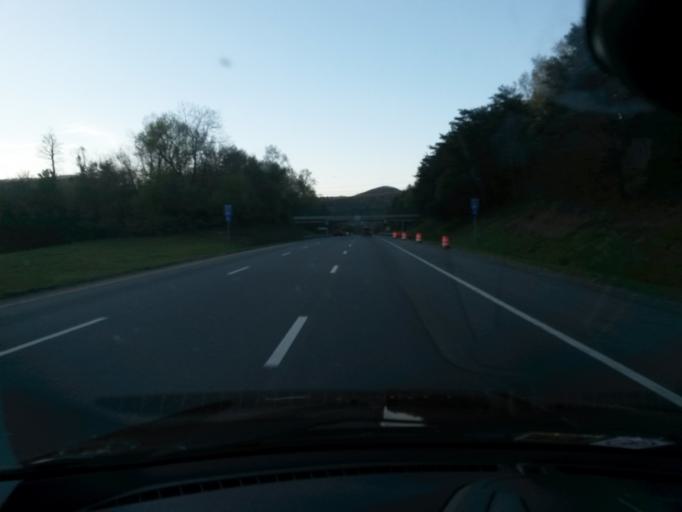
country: US
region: Virginia
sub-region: Roanoke County
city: Hollins
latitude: 37.3348
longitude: -79.9943
